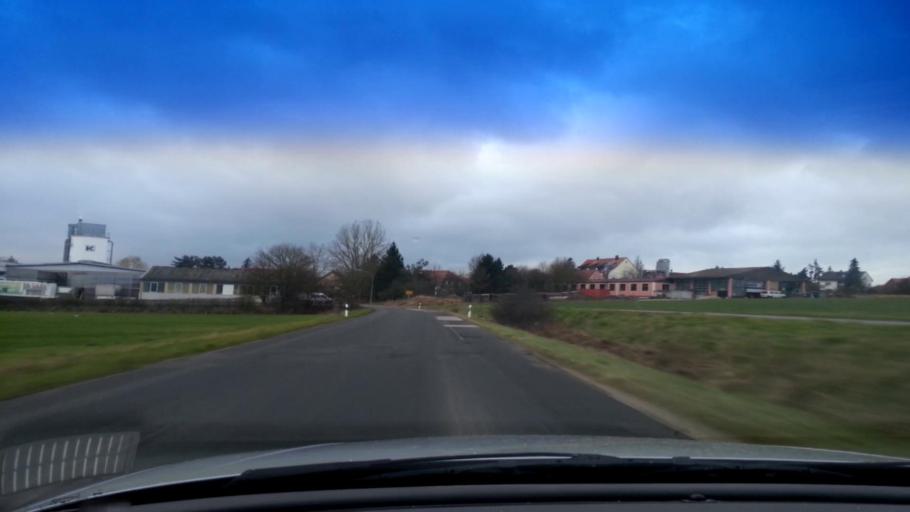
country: DE
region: Bavaria
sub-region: Upper Franconia
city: Burgebrach
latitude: 49.8361
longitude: 10.7667
